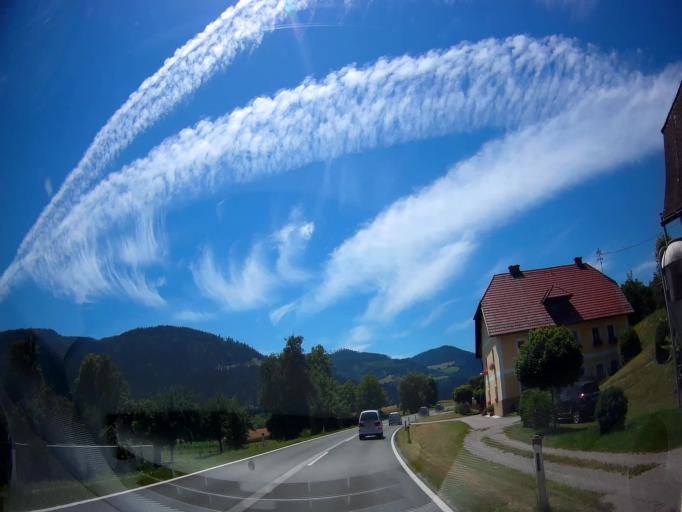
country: AT
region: Carinthia
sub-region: Politischer Bezirk Sankt Veit an der Glan
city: Strassburg
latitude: 46.9022
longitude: 14.3675
